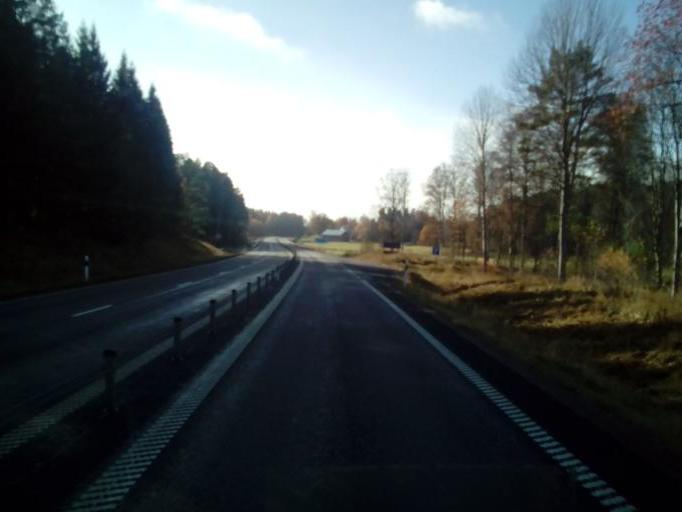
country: SE
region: Kalmar
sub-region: Vimmerby Kommun
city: Vimmerby
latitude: 57.7008
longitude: 16.0171
